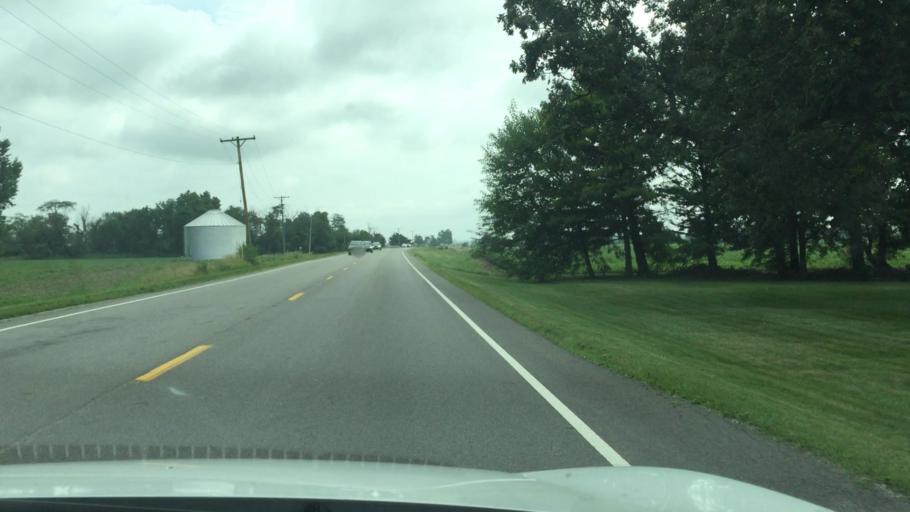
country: US
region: Ohio
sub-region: Union County
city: Marysville
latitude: 40.1588
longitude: -83.4524
